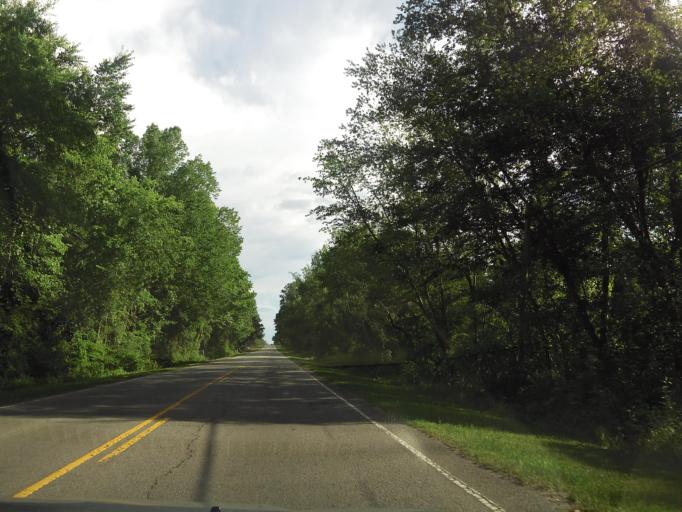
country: US
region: South Carolina
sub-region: Hampton County
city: Estill
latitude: 32.8103
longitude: -81.2400
